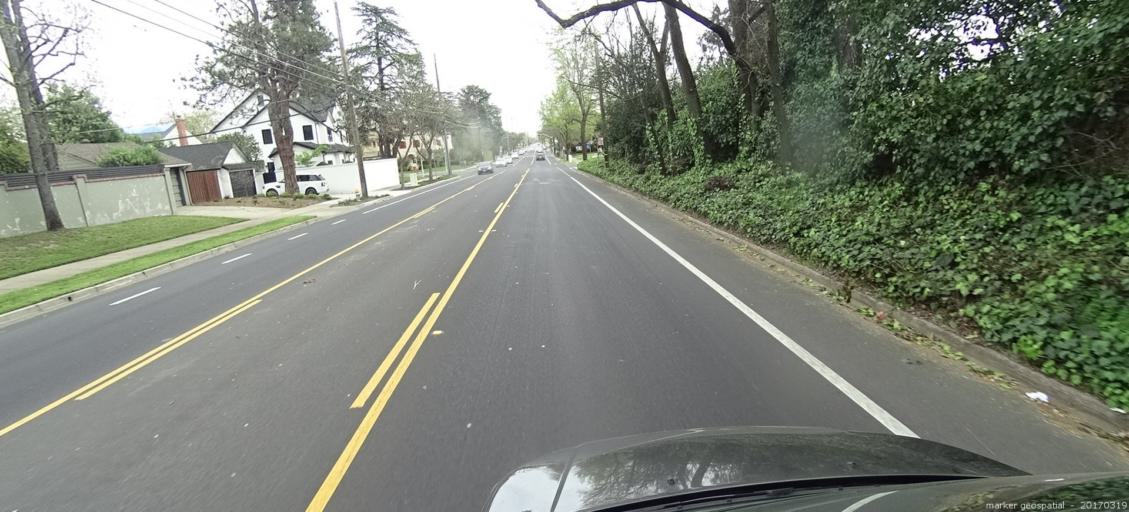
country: US
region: California
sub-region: Sacramento County
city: Sacramento
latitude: 38.5628
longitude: -121.4495
